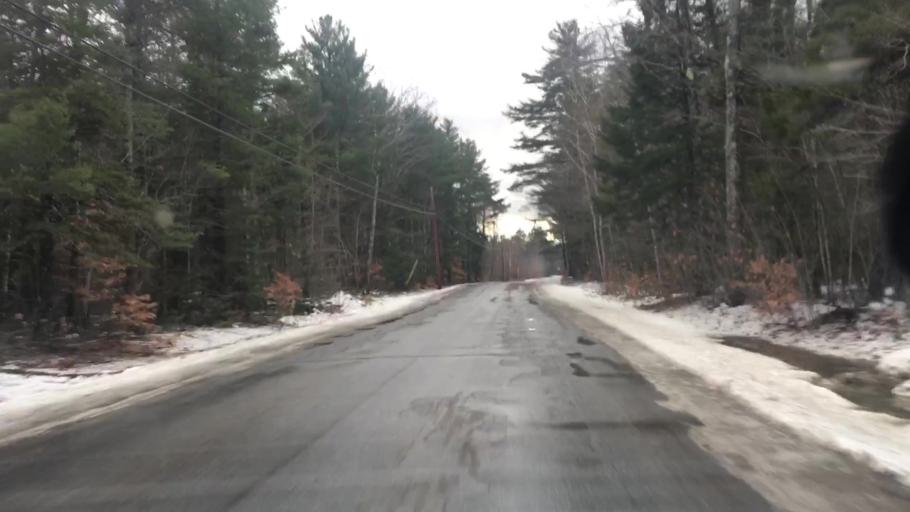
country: US
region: Maine
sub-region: Hancock County
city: Dedham
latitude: 44.6489
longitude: -68.7044
